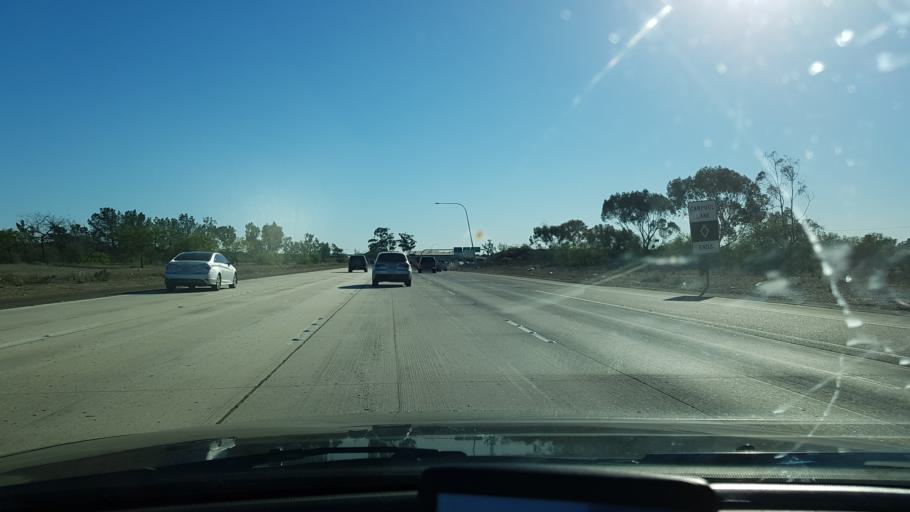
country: US
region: California
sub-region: San Diego County
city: La Mesa
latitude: 32.8588
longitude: -117.1145
